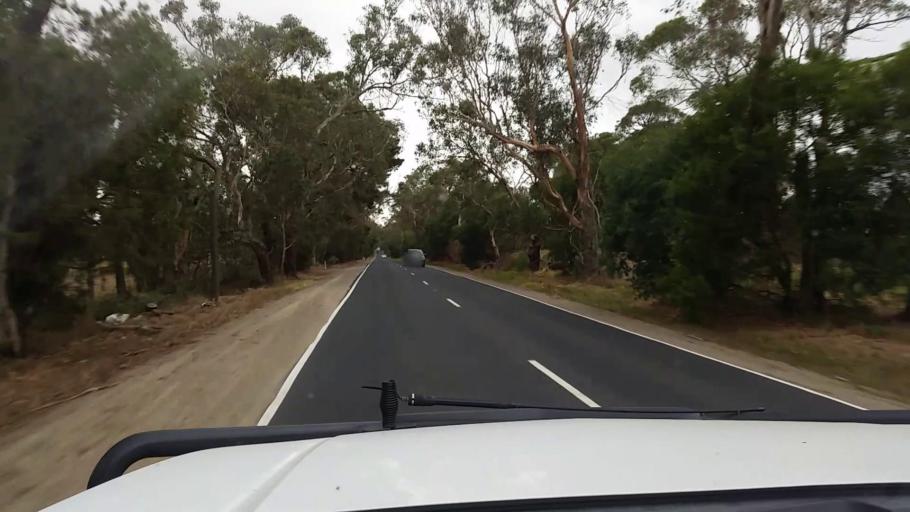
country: AU
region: Victoria
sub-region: Mornington Peninsula
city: Somerville
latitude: -38.2329
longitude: 145.1519
